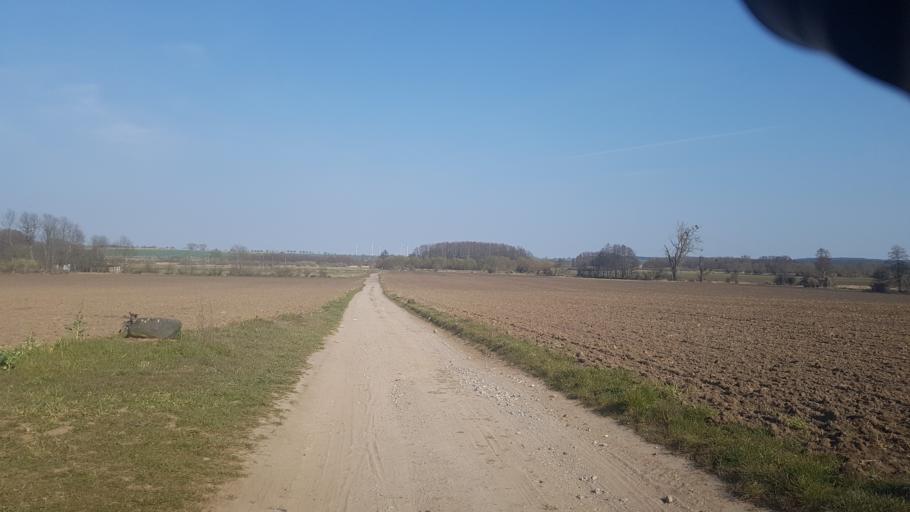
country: DE
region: Brandenburg
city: Prenzlau
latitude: 53.2245
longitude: 13.8445
